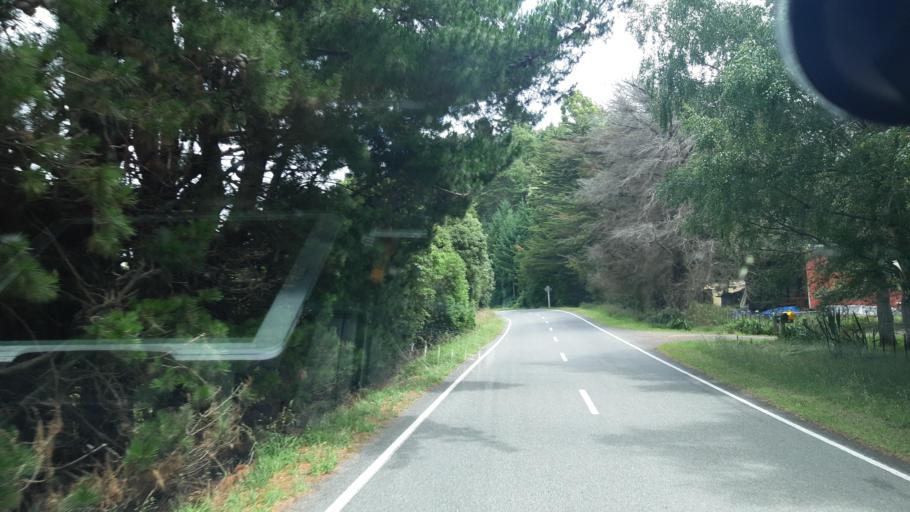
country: NZ
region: Marlborough
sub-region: Marlborough District
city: Blenheim
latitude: -41.4864
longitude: 173.7595
